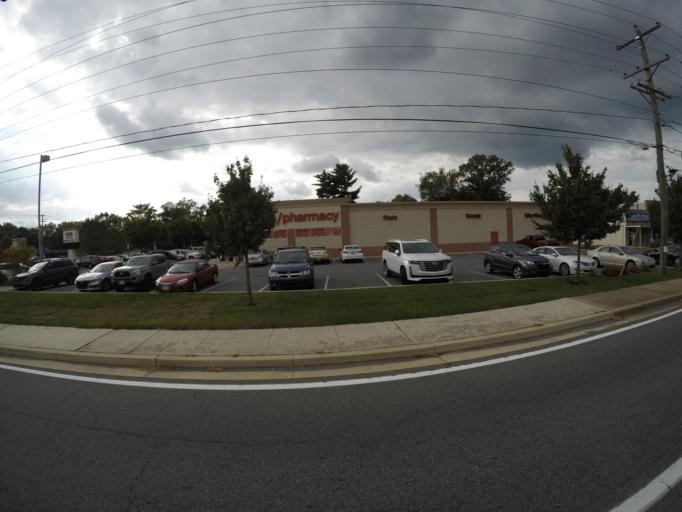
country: US
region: Delaware
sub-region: New Castle County
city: Brookside
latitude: 39.6631
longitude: -75.7267
